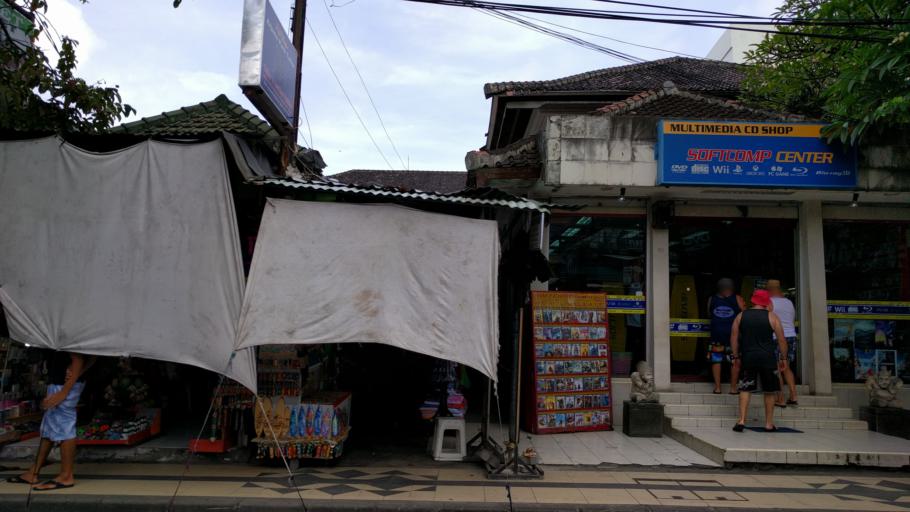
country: ID
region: Bali
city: Jabajero
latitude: -8.7310
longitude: 115.1677
